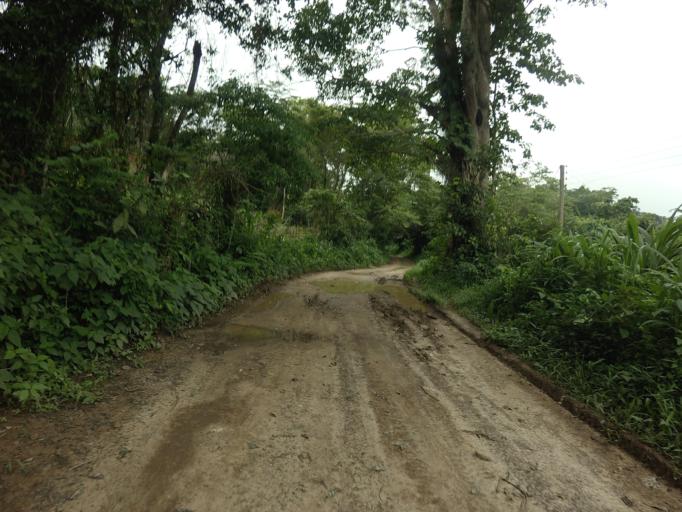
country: TG
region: Plateaux
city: Kpalime
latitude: 6.8437
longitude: 0.4435
